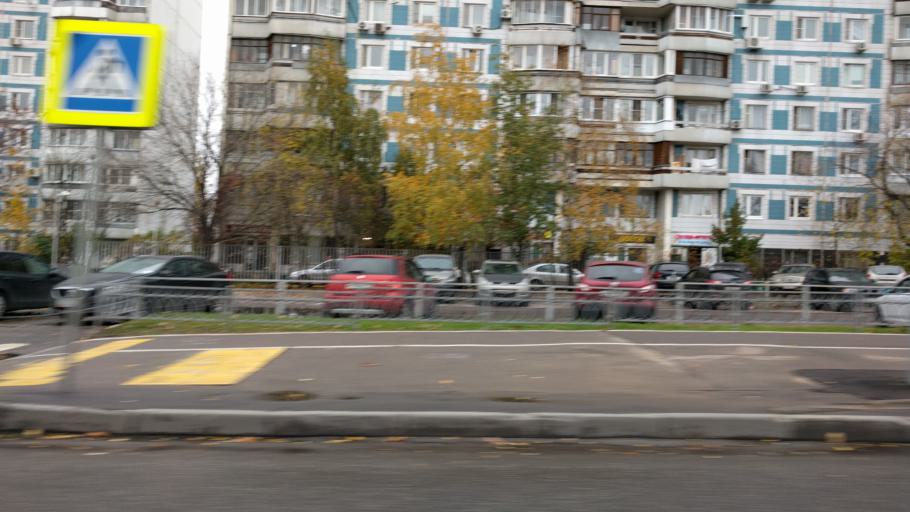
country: RU
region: Moskovskaya
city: Bol'shaya Setun'
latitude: 55.7483
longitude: 37.4164
